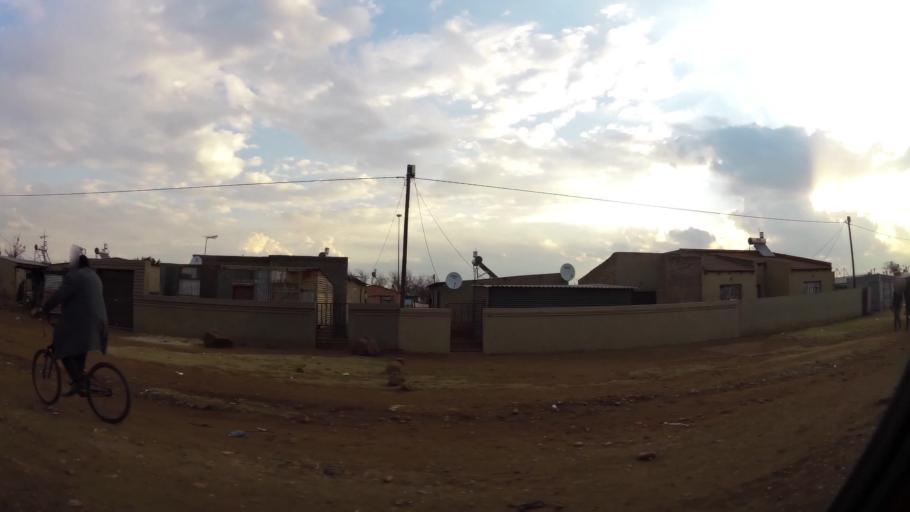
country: ZA
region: Gauteng
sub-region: City of Johannesburg Metropolitan Municipality
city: Orange Farm
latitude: -26.5599
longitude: 27.8320
